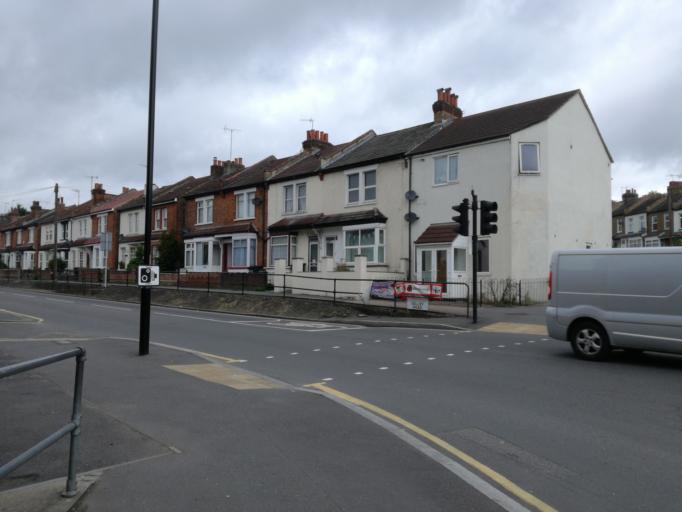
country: GB
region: England
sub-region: Greater London
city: Coulsdon
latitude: 51.3199
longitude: -0.1407
